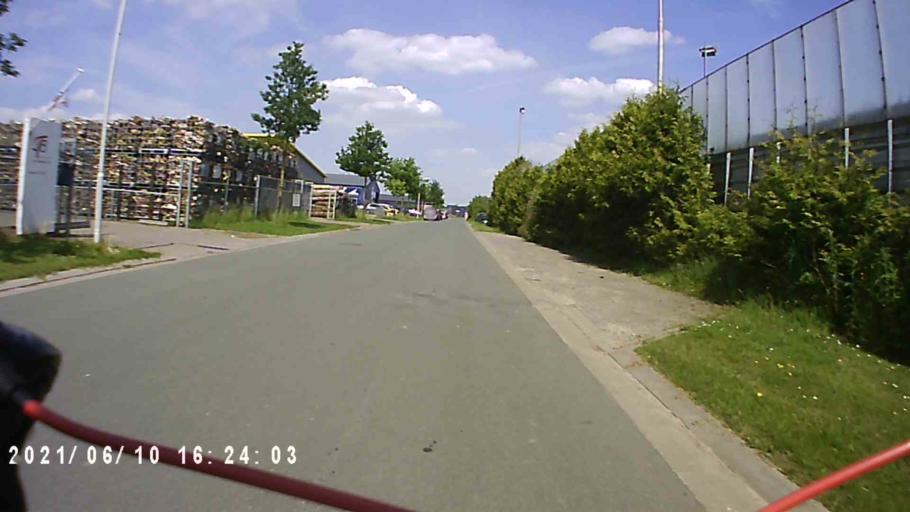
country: NL
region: Friesland
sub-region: Gemeente Achtkarspelen
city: Drogeham
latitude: 53.2189
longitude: 6.1083
